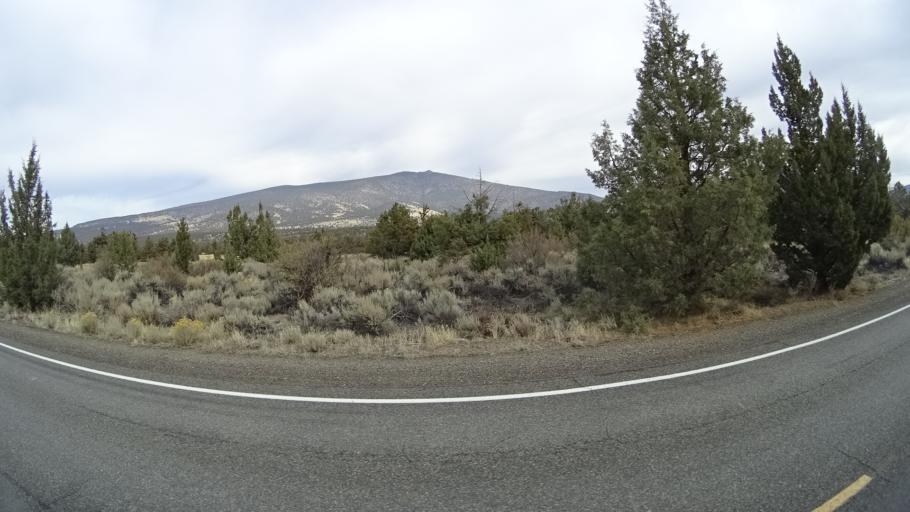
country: US
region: California
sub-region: Siskiyou County
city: Weed
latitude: 41.5783
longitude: -122.2858
